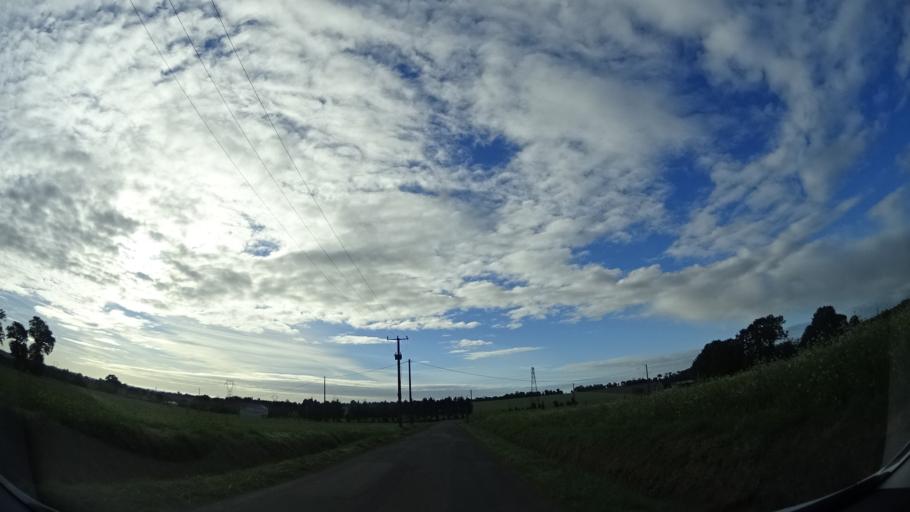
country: FR
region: Brittany
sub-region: Departement d'Ille-et-Vilaine
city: Geveze
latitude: 48.2042
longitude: -1.8066
